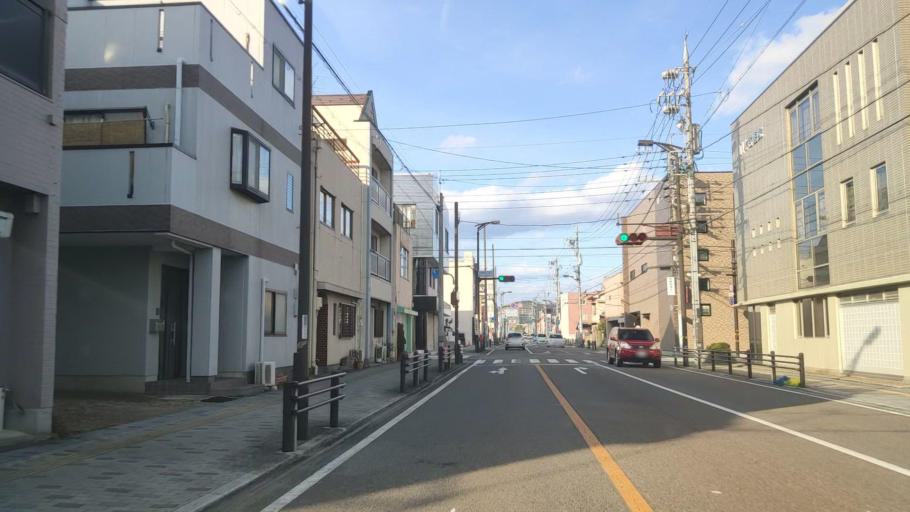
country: JP
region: Gifu
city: Gifu-shi
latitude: 35.4015
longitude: 136.7575
